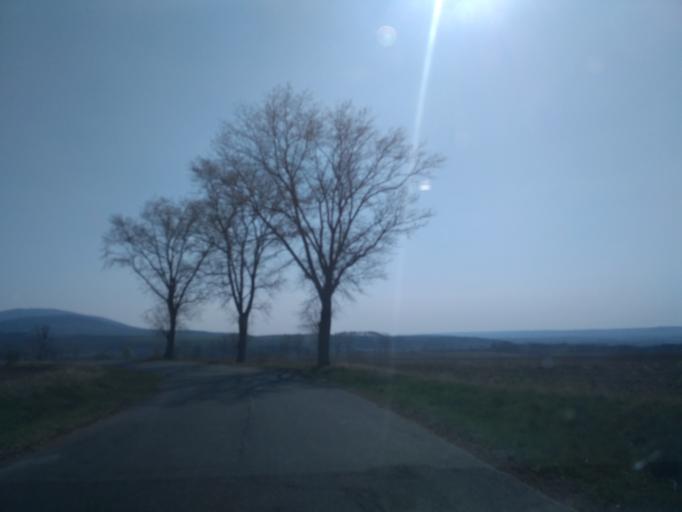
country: HU
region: Borsod-Abauj-Zemplen
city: Gonc
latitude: 48.5382
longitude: 21.3360
